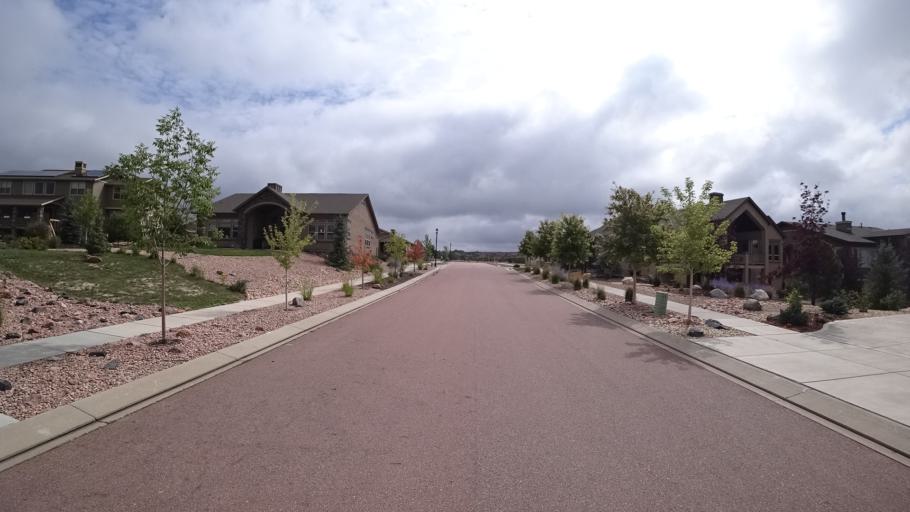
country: US
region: Colorado
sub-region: El Paso County
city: Gleneagle
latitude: 39.0140
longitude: -104.7877
